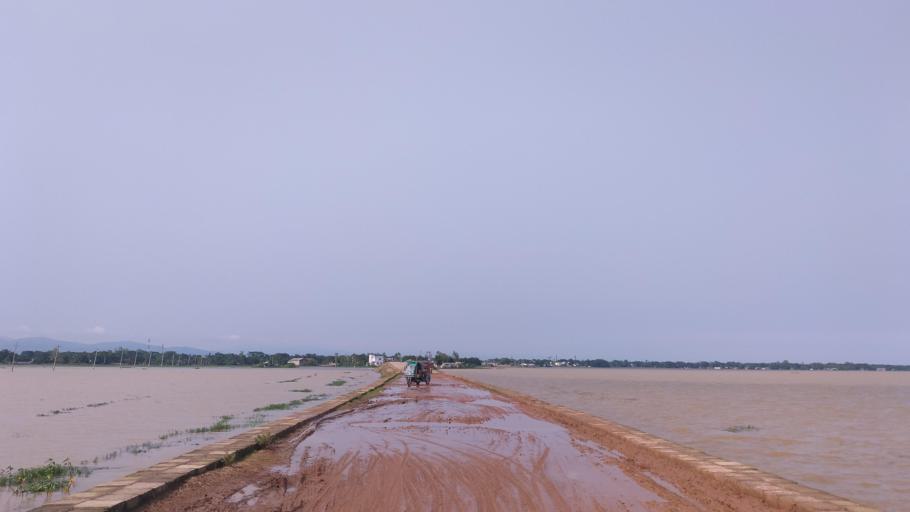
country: BD
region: Dhaka
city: Netrakona
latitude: 25.0654
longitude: 90.8804
